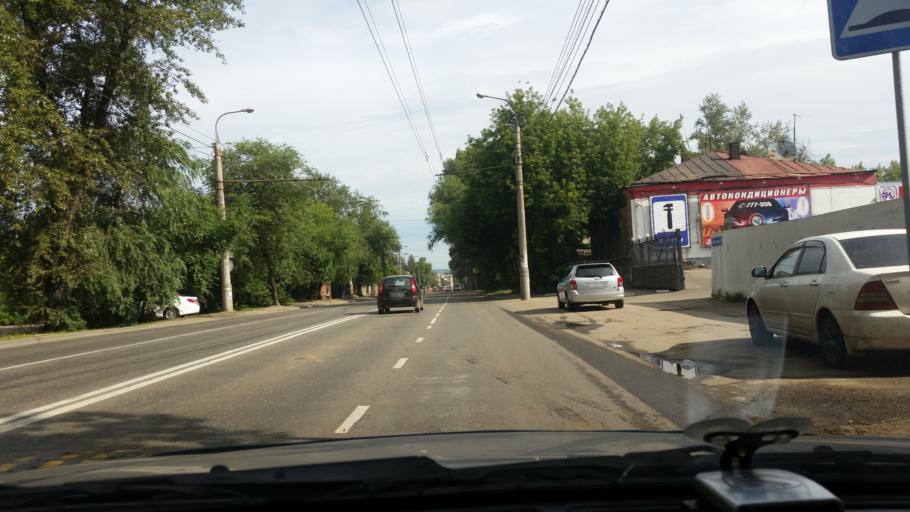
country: RU
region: Irkutsk
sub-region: Irkutskiy Rayon
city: Irkutsk
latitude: 52.3037
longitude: 104.2985
